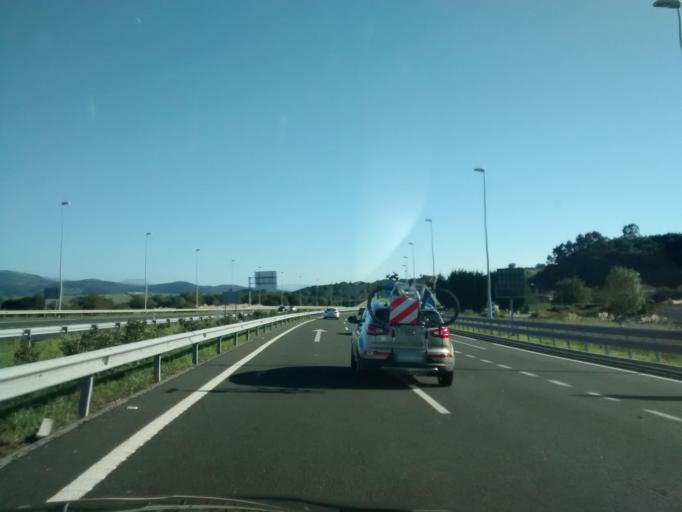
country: ES
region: Cantabria
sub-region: Provincia de Cantabria
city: Camargo
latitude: 43.4250
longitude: -3.8718
